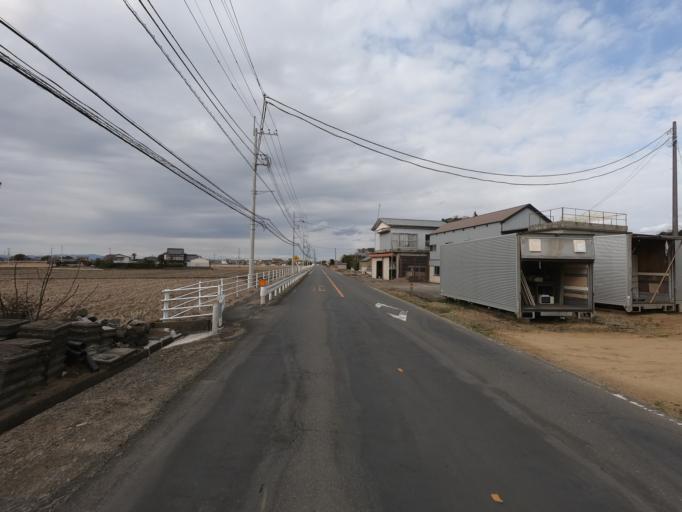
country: JP
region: Ibaraki
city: Inashiki
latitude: 36.0774
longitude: 140.4261
